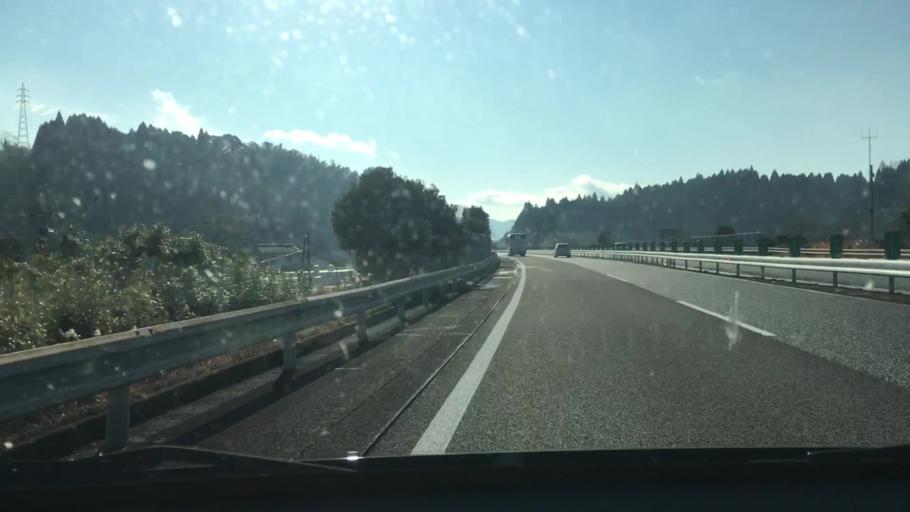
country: JP
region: Kagoshima
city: Okuchi-shinohara
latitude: 32.0216
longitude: 130.7751
